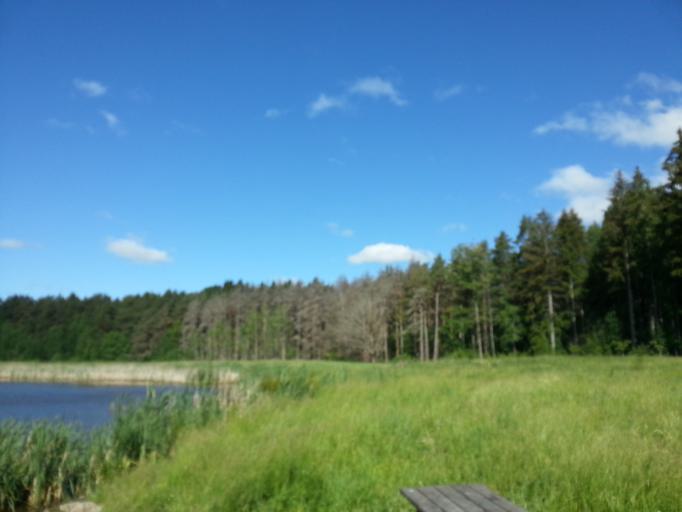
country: SE
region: OEstergoetland
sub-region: Norrkopings Kommun
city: Norrkoping
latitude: 58.5658
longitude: 16.1988
